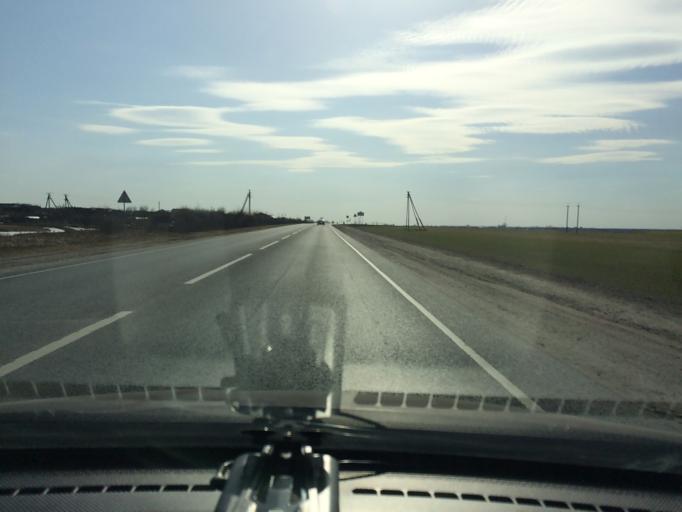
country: RU
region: Mariy-El
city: Yoshkar-Ola
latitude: 56.6697
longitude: 47.9999
